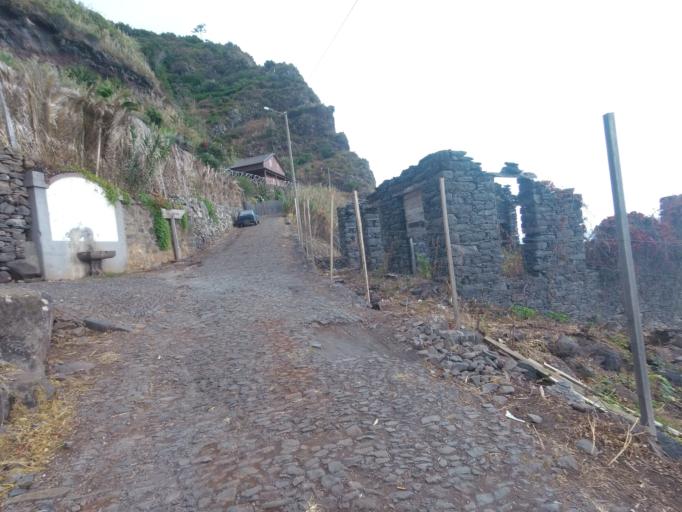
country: PT
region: Madeira
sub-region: Santana
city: Santana
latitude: 32.8304
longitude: -16.8987
